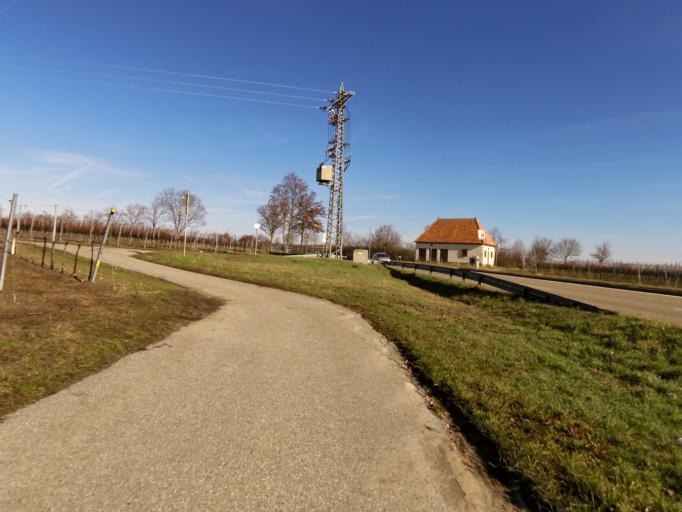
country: DE
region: Rheinland-Pfalz
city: Kallstadt
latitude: 49.4821
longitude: 8.1879
